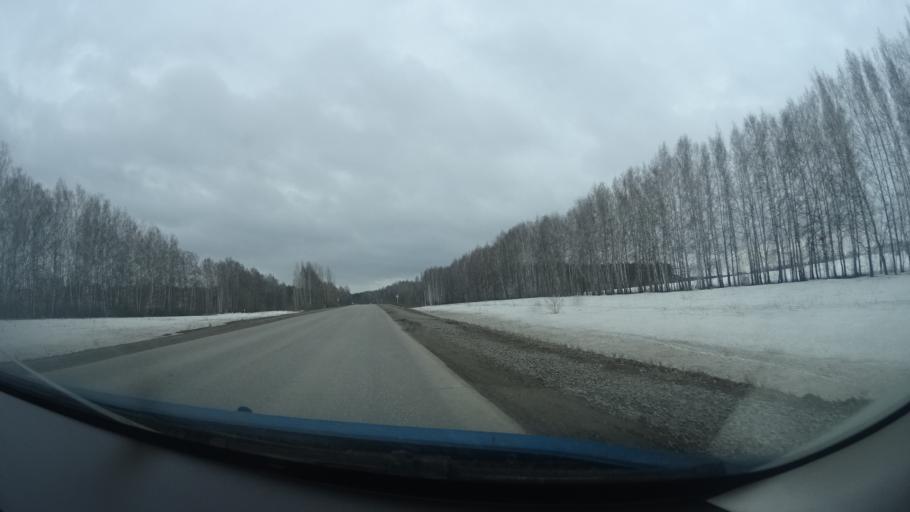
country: RU
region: Bashkortostan
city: Birsk
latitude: 55.3410
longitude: 55.5927
